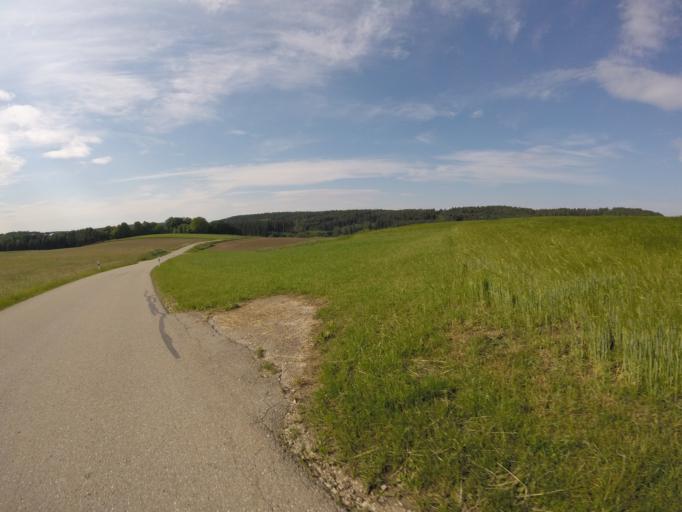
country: DE
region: Bavaria
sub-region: Upper Bavaria
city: Scheyern
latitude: 48.4687
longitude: 11.4672
